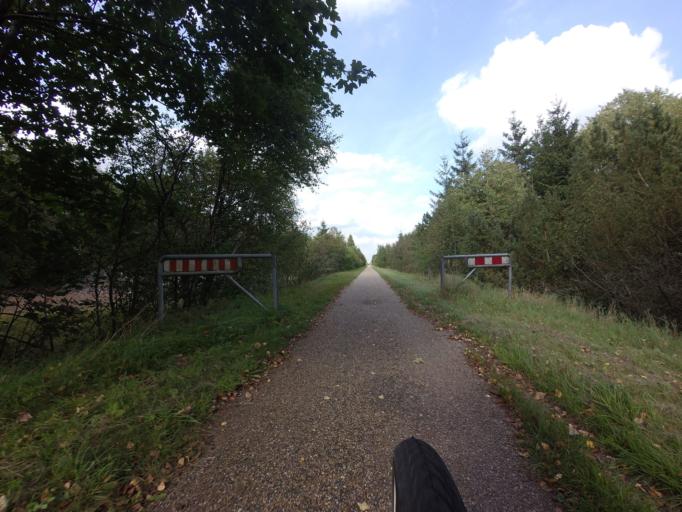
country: DK
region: Central Jutland
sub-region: Viborg Kommune
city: Karup
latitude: 56.2468
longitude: 9.0999
